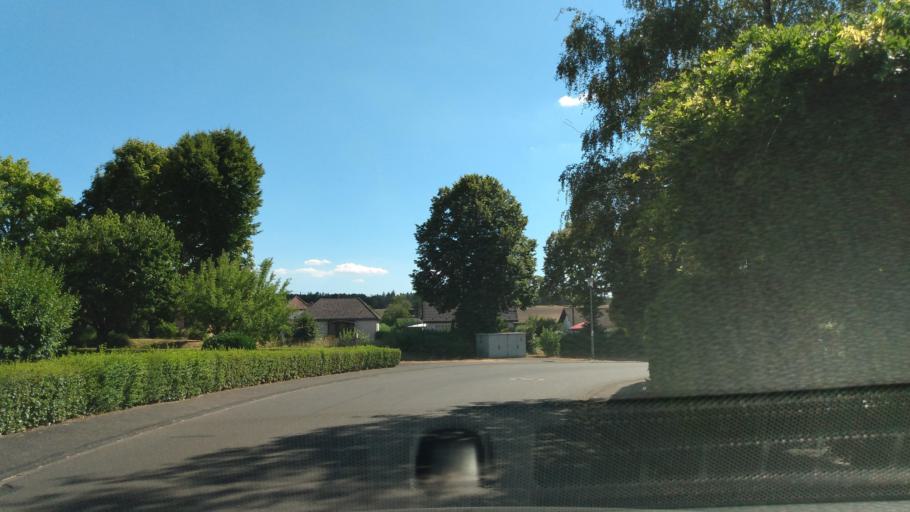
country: DE
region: Rheinland-Pfalz
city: Hupperath
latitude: 49.9988
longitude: 6.8397
